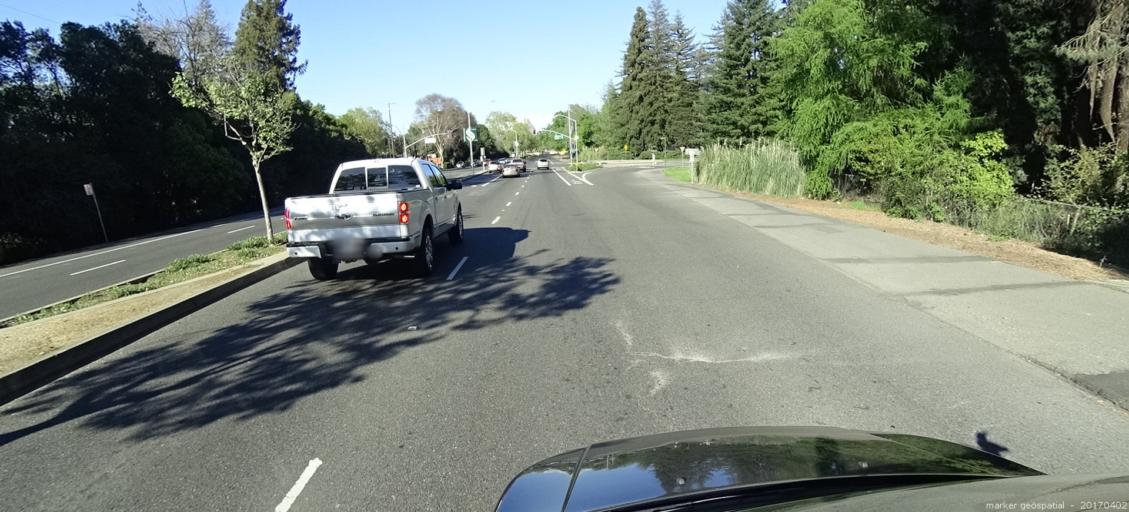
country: US
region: California
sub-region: Sacramento County
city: Arden-Arcade
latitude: 38.5656
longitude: -121.4293
